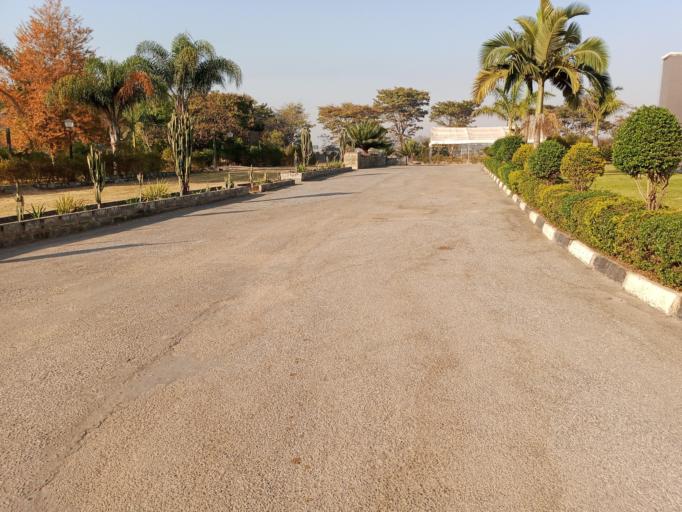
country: ZM
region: Copperbelt
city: Kitwe
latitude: -12.8748
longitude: 28.2544
